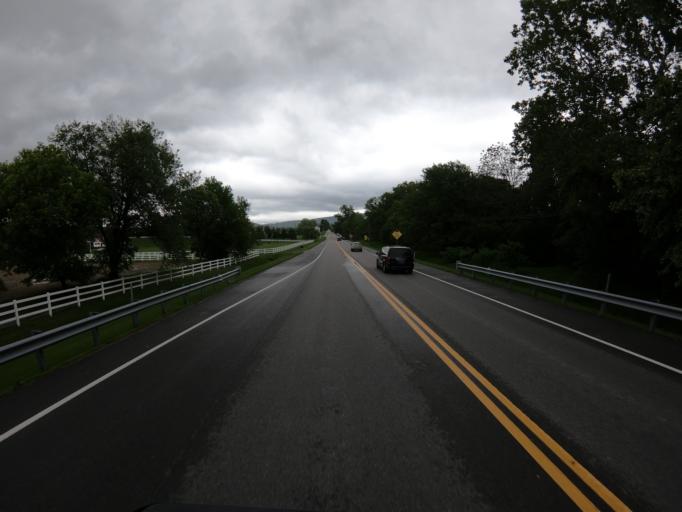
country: US
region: Maryland
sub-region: Washington County
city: Boonsboro
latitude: 39.5028
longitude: -77.6639
